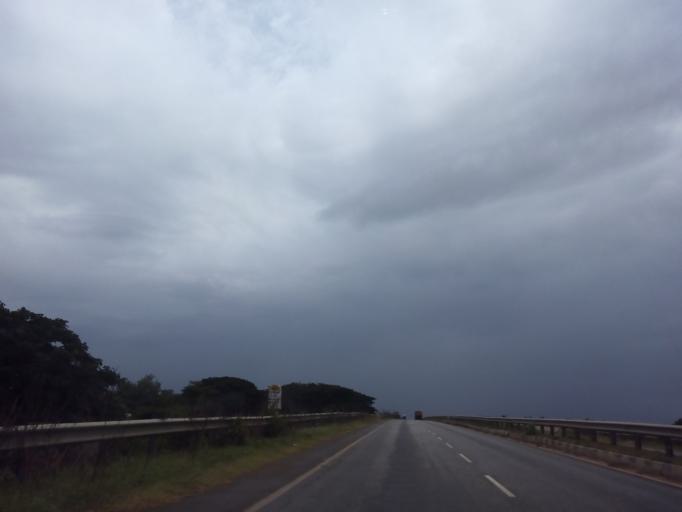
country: IN
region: Karnataka
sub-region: Davanagere
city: Harihar
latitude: 14.4705
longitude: 75.8339
